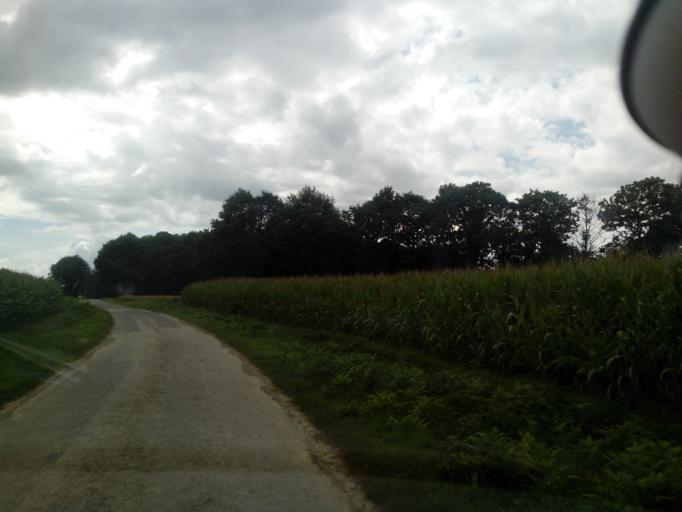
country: FR
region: Brittany
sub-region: Departement du Morbihan
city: Mauron
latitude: 48.1050
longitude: -2.3566
